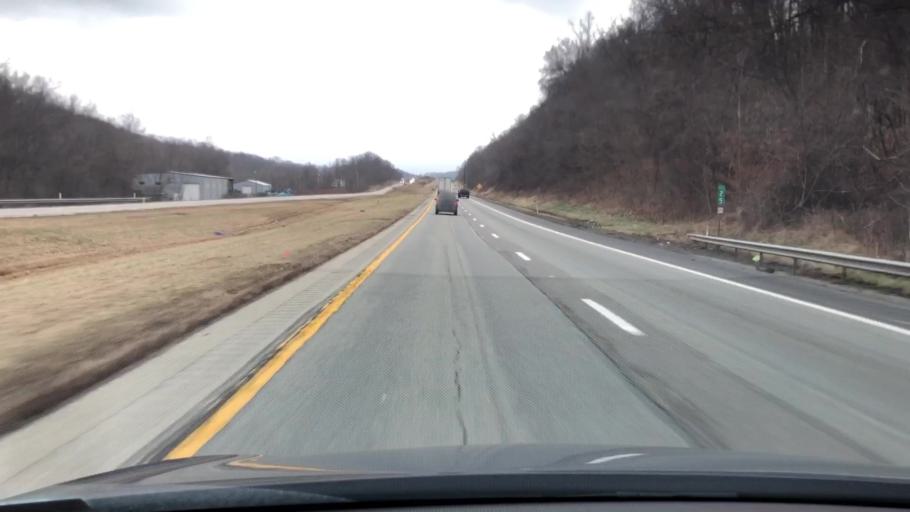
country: US
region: Pennsylvania
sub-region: Washington County
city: East Washington
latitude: 40.0437
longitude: -80.1819
